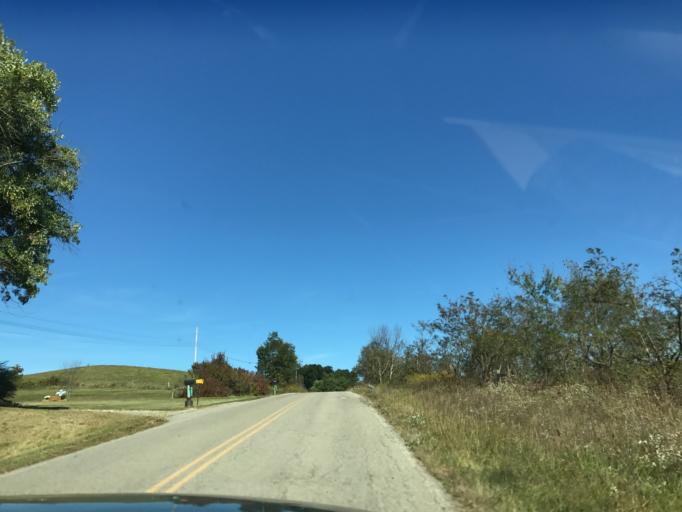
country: US
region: Ohio
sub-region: Belmont County
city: Barnesville
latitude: 40.0582
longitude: -81.3119
